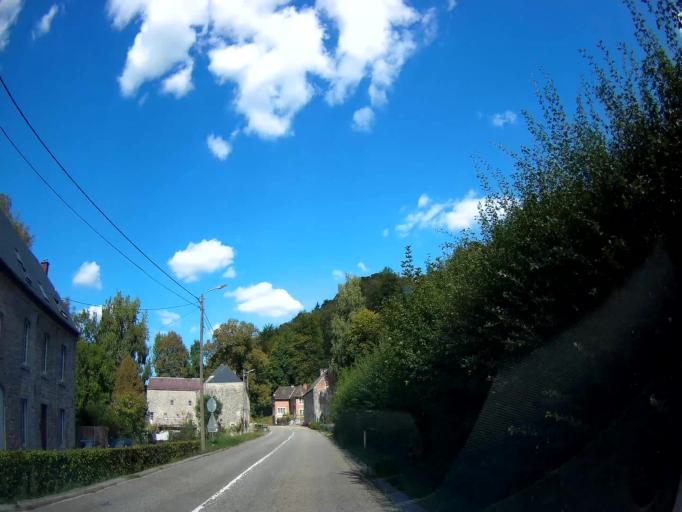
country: BE
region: Wallonia
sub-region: Province de Namur
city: Houyet
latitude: 50.2210
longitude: 4.9854
